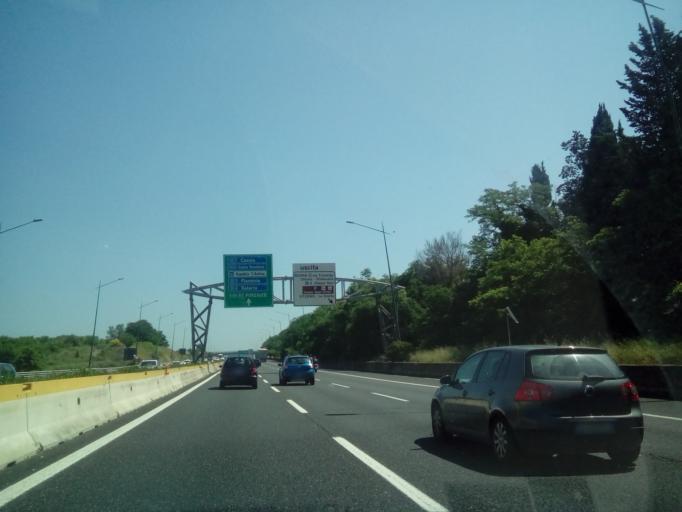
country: IT
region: Latium
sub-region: Citta metropolitana di Roma Capitale
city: Valle Santa
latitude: 41.9622
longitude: 12.3934
